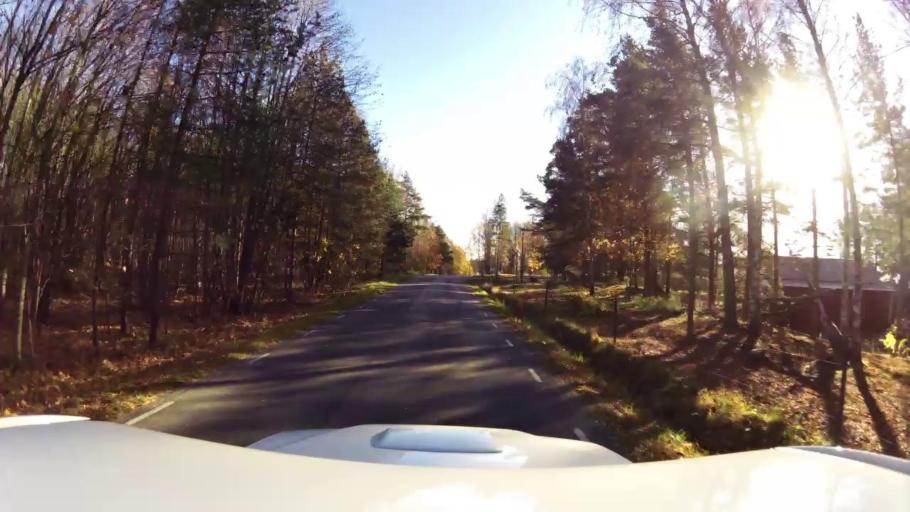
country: SE
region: OEstergoetland
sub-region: Linkopings Kommun
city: Linkoping
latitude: 58.3477
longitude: 15.6024
